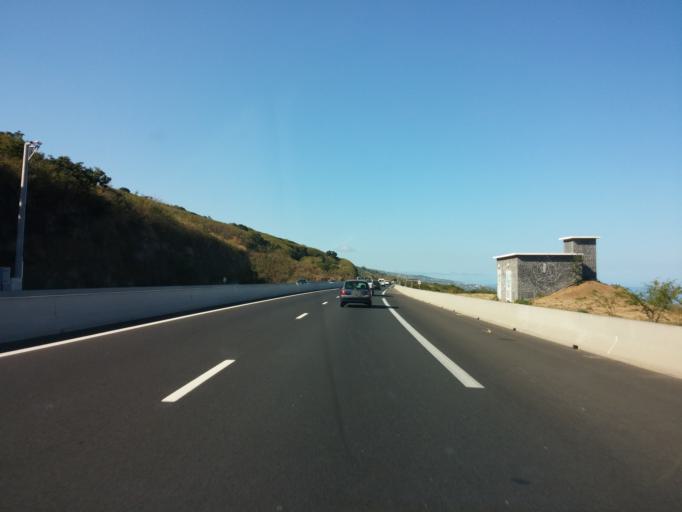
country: RE
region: Reunion
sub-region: Reunion
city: Trois-Bassins
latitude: -21.1196
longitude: 55.2786
